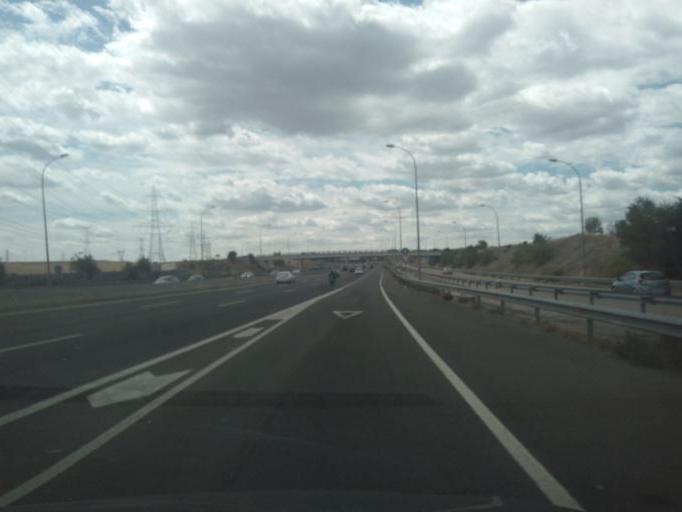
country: ES
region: Madrid
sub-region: Provincia de Madrid
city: San Sebastian de los Reyes
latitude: 40.5597
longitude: -3.6002
